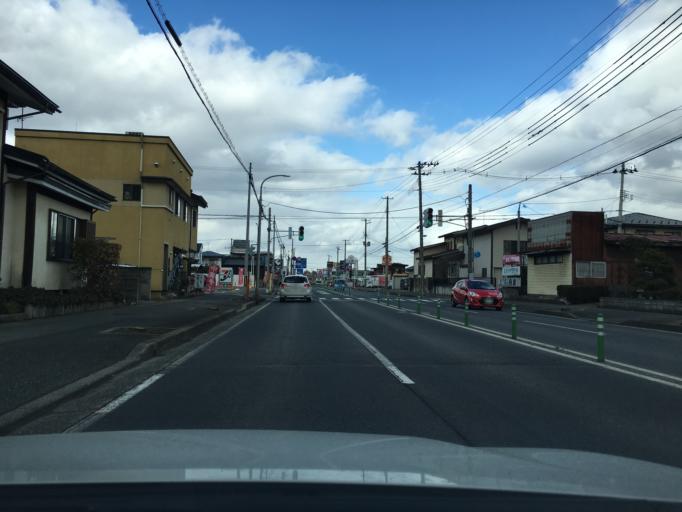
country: JP
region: Yamagata
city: Yamagata-shi
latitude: 38.2348
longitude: 140.3058
